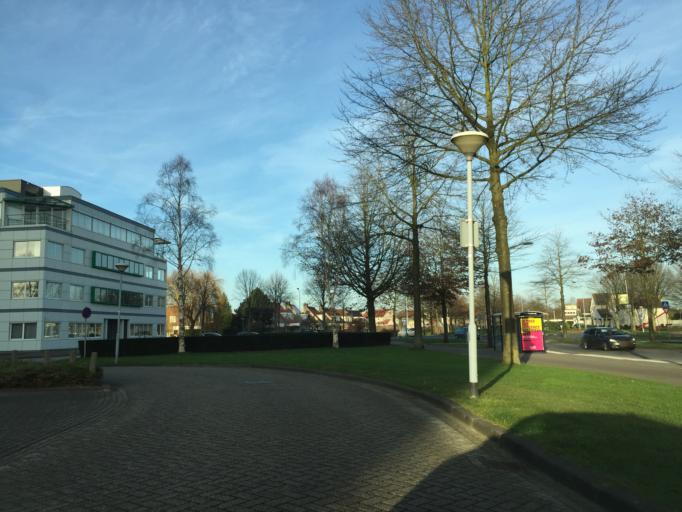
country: NL
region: North Brabant
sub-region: Gemeente 's-Hertogenbosch
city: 's-Hertogenbosch
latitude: 51.7238
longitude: 5.2949
